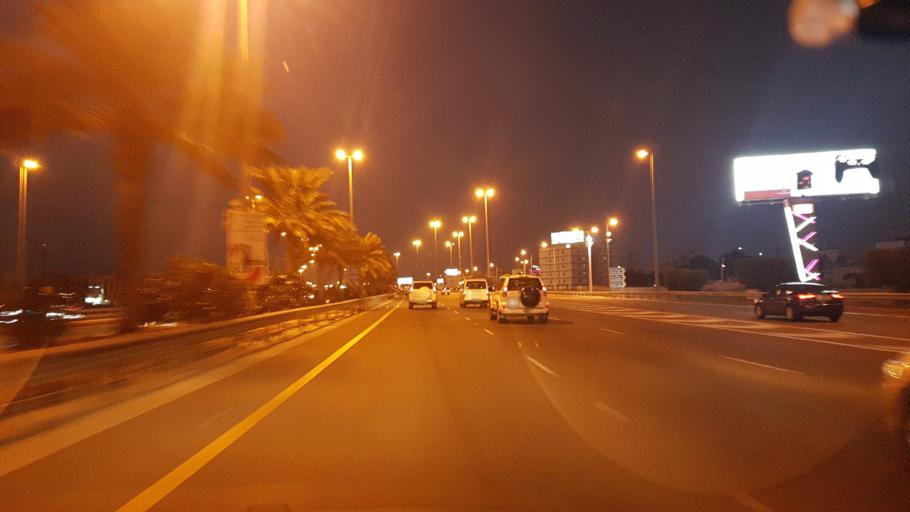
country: BH
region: Manama
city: Jidd Hafs
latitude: 26.2123
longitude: 50.5193
